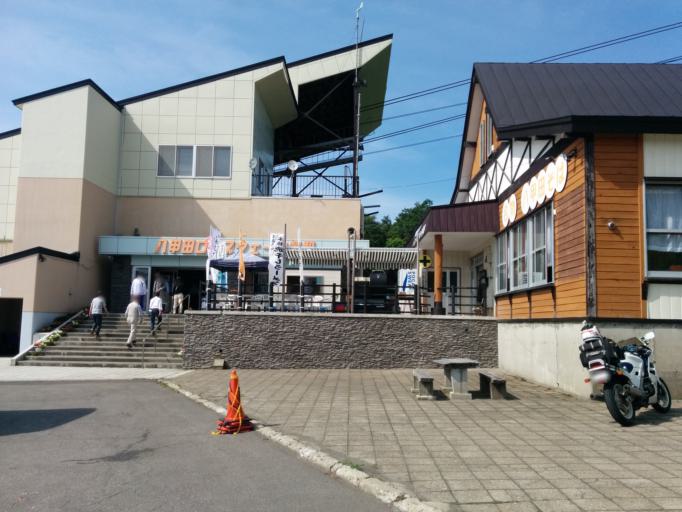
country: JP
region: Aomori
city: Aomori Shi
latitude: 40.6806
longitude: 140.8318
